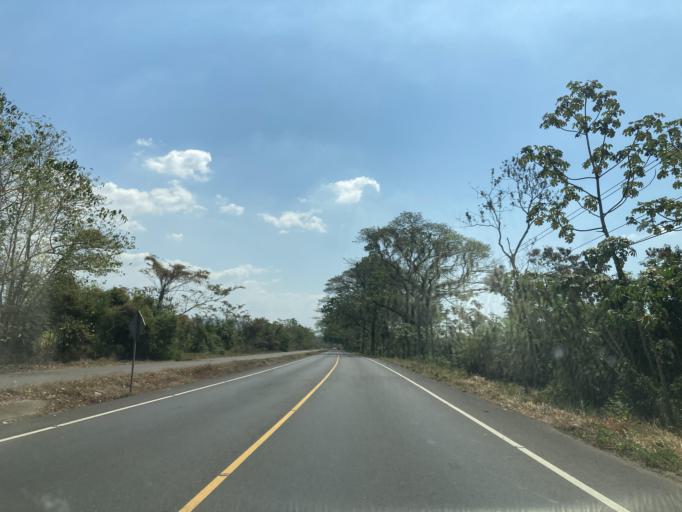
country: GT
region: Escuintla
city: Guanagazapa
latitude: 14.1780
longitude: -90.6855
